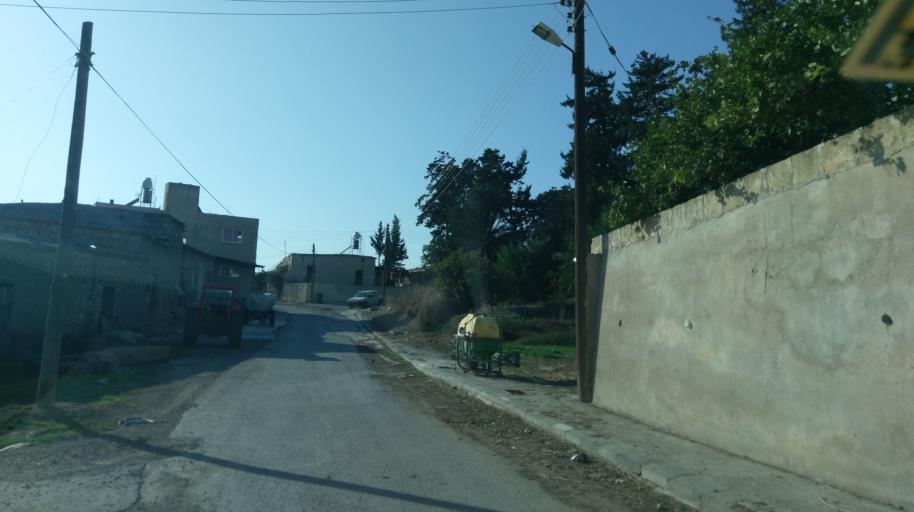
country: CY
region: Ammochostos
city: Leonarisso
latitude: 35.4779
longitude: 34.1075
